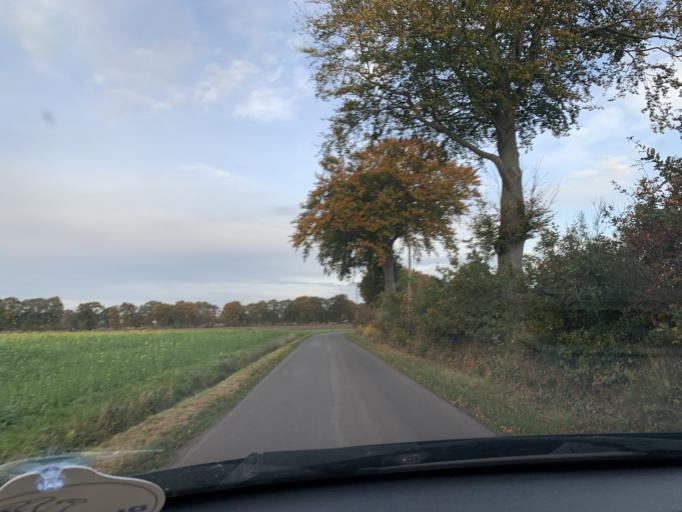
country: DE
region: Lower Saxony
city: Wiefelstede
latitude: 53.2579
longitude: 8.0909
